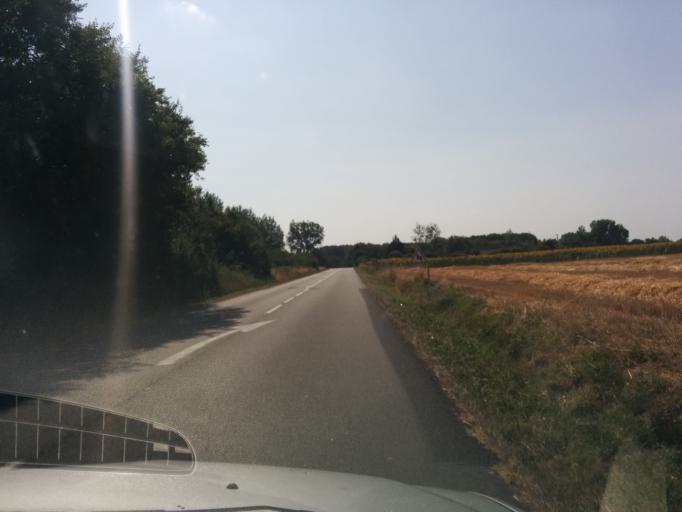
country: FR
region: Poitou-Charentes
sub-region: Departement de la Vienne
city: Saint-Jean-de-Sauves
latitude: 46.8057
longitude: 0.0396
